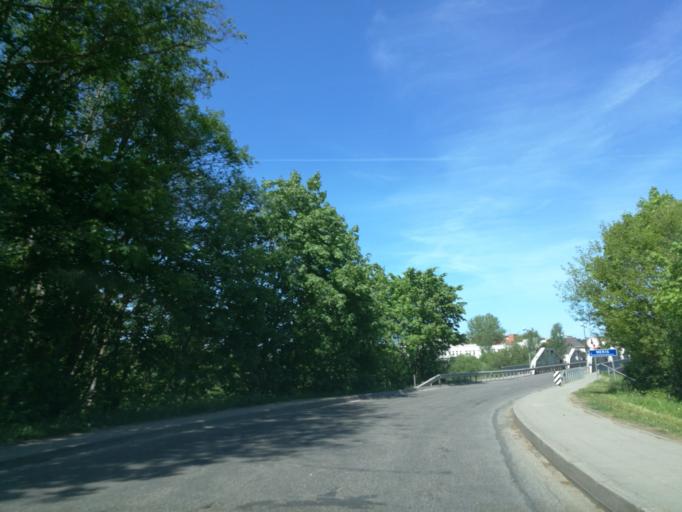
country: LT
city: Nemencine
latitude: 54.8442
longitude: 25.4628
